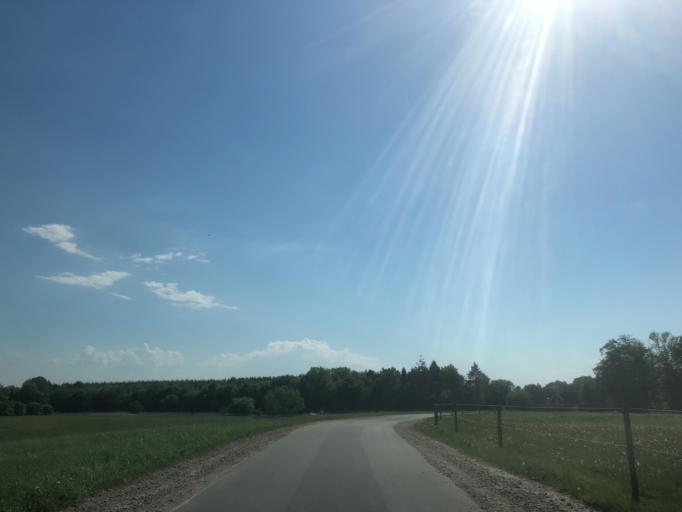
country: DK
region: Zealand
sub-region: Roskilde Kommune
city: Vindinge
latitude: 55.6184
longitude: 12.1190
